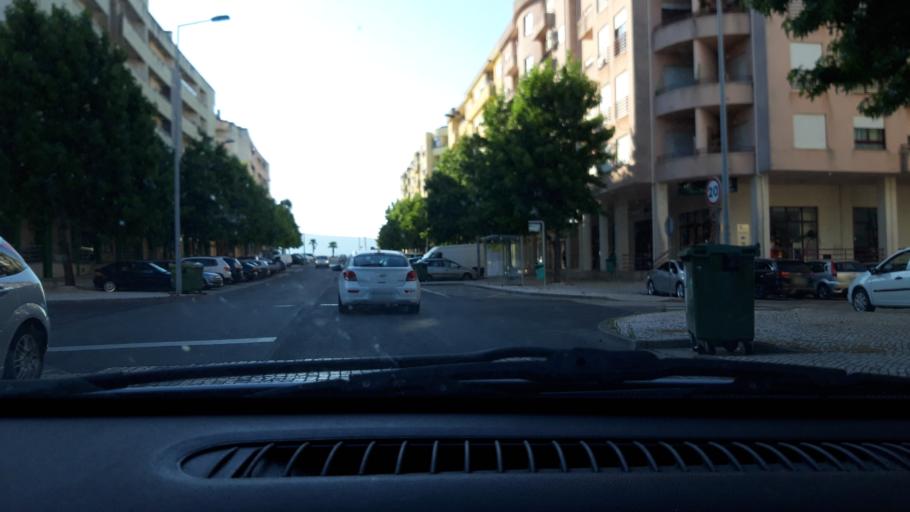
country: PT
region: Santarem
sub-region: Torres Novas
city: Torres Novas
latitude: 39.4753
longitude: -8.5487
